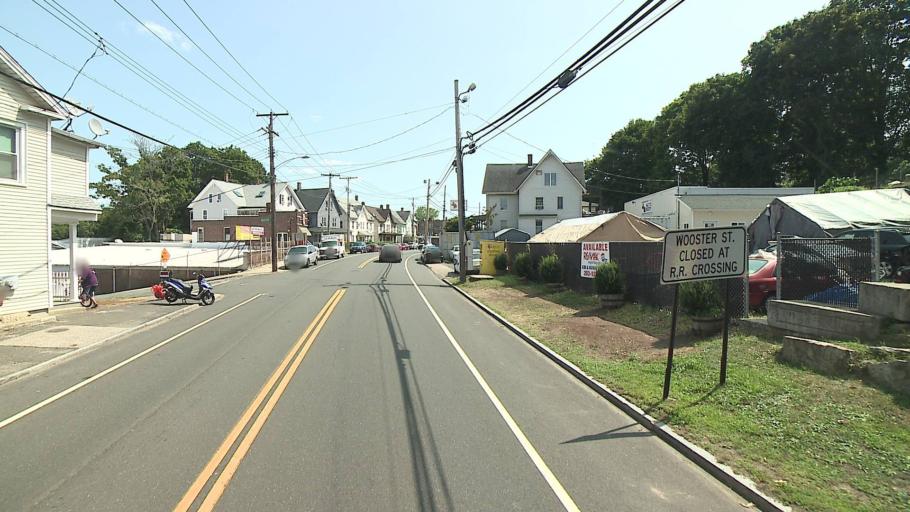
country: US
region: Connecticut
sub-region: Fairfield County
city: Shelton
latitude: 41.3200
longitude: -73.0970
